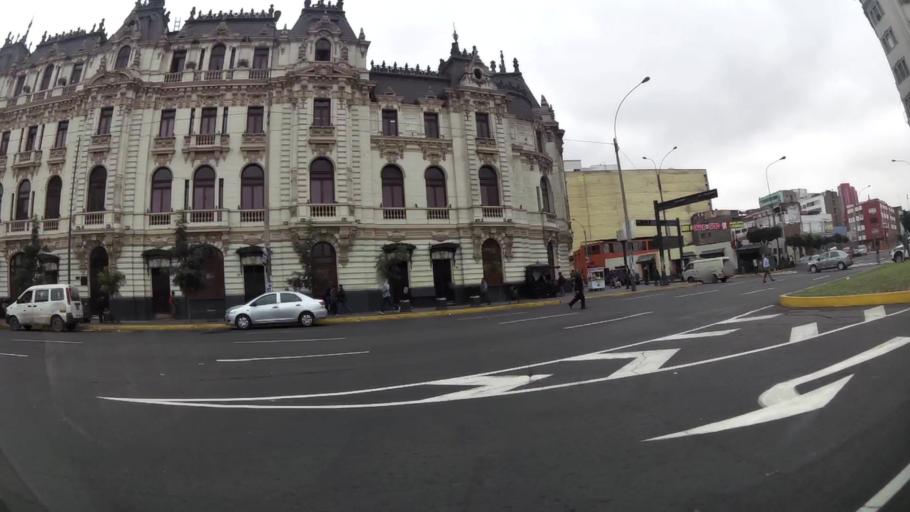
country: PE
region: Lima
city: Lima
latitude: -12.0557
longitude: -77.0363
